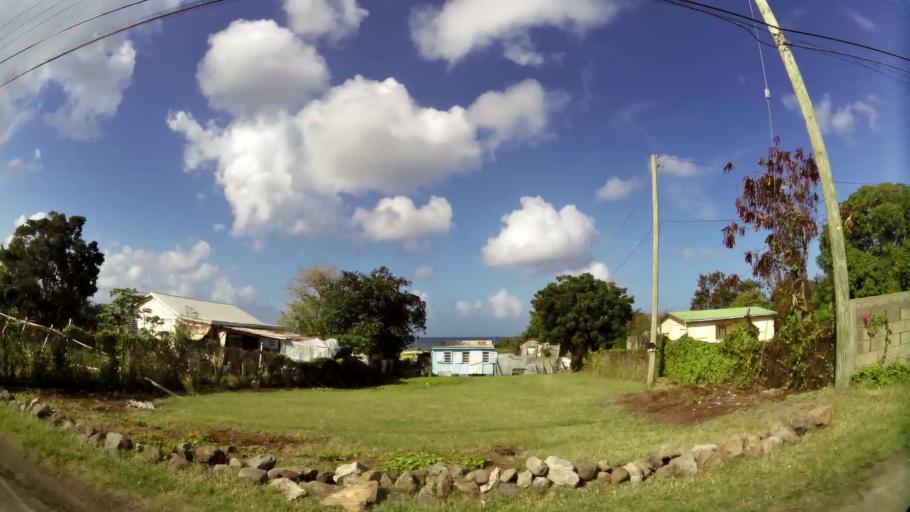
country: KN
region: Saint Paul Charlestown
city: Charlestown
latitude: 17.1273
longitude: -62.6268
